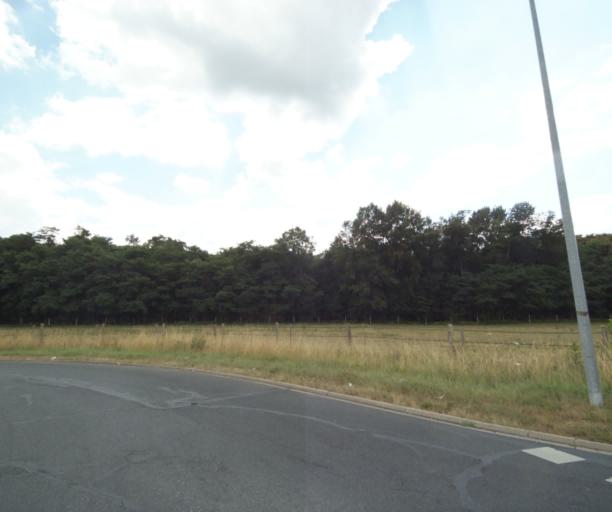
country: FR
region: Ile-de-France
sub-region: Departement de Seine-et-Marne
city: Vulaines-sur-Seine
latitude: 48.4227
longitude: 2.7689
